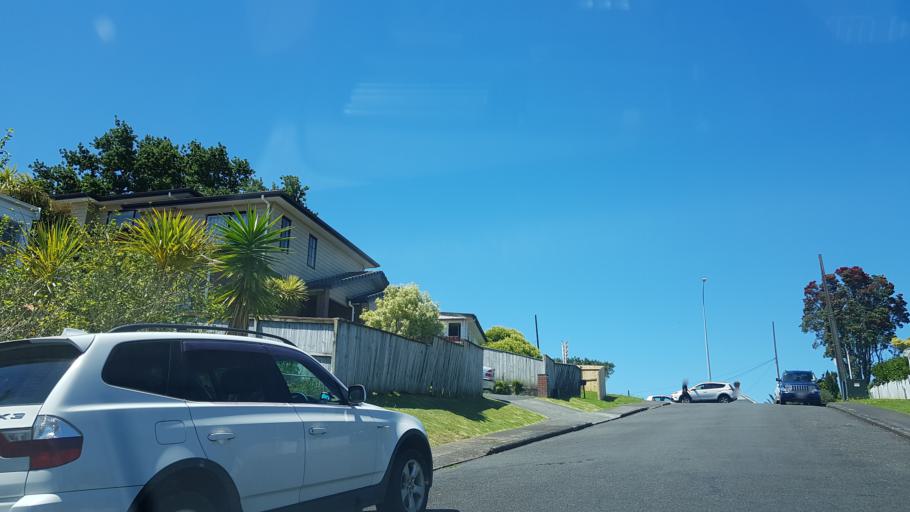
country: NZ
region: Auckland
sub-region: Auckland
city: North Shore
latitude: -36.8108
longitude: 174.7197
